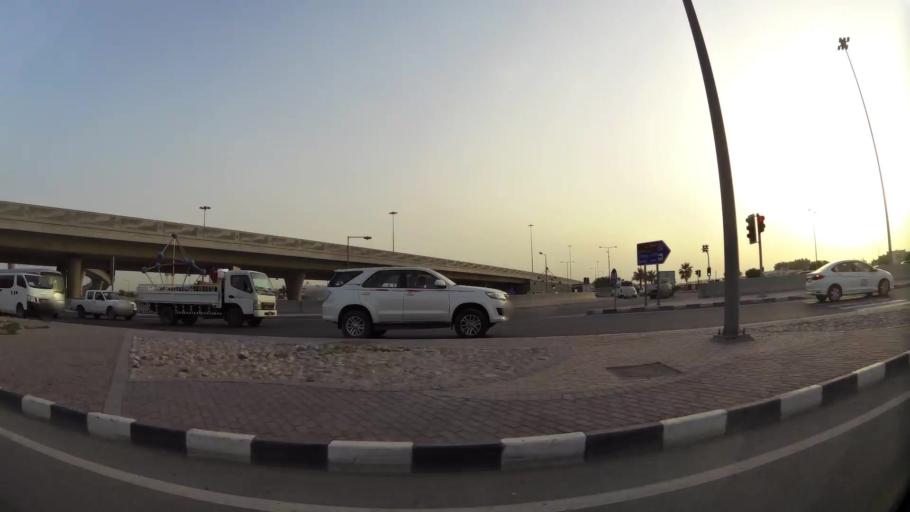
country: QA
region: Baladiyat ar Rayyan
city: Ar Rayyan
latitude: 25.2263
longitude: 51.4320
